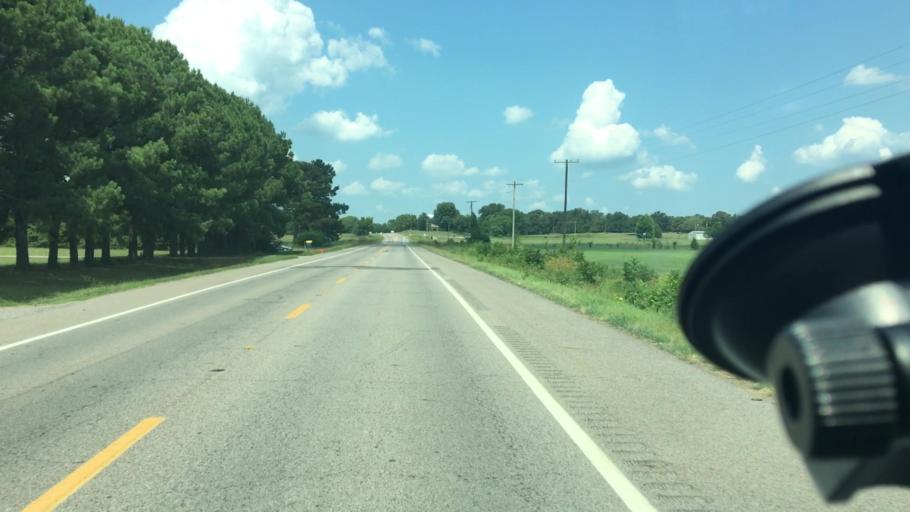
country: US
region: Arkansas
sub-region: Logan County
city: Paris
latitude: 35.2951
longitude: -93.6813
